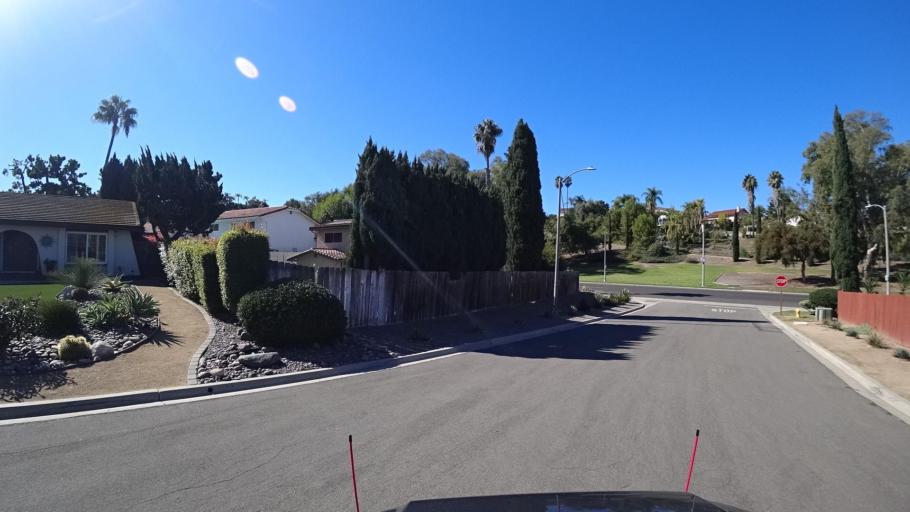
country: US
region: California
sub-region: San Diego County
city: Bonita
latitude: 32.6701
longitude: -117.0105
